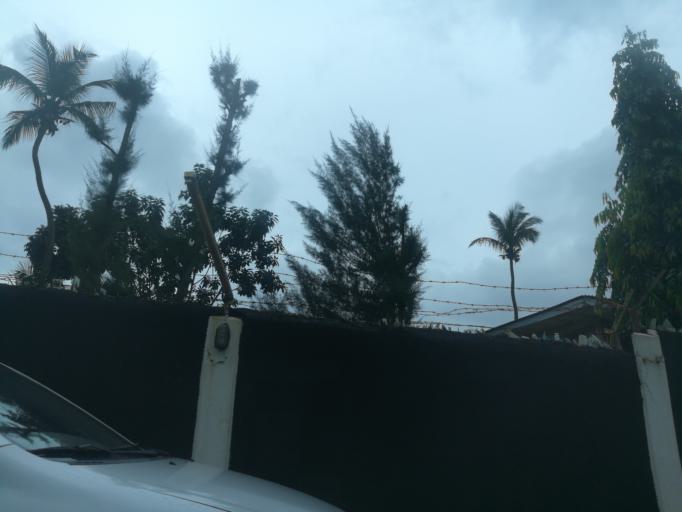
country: NG
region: Lagos
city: Ikeja
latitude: 6.6131
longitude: 3.3470
